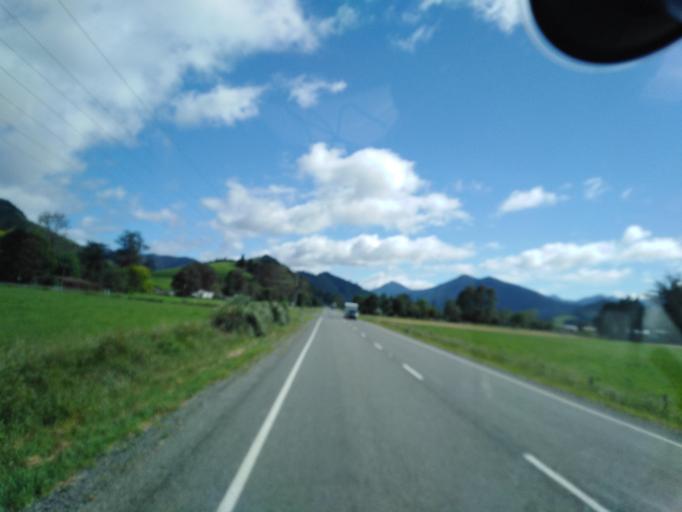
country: NZ
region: Nelson
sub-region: Nelson City
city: Nelson
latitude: -41.2400
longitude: 173.5792
